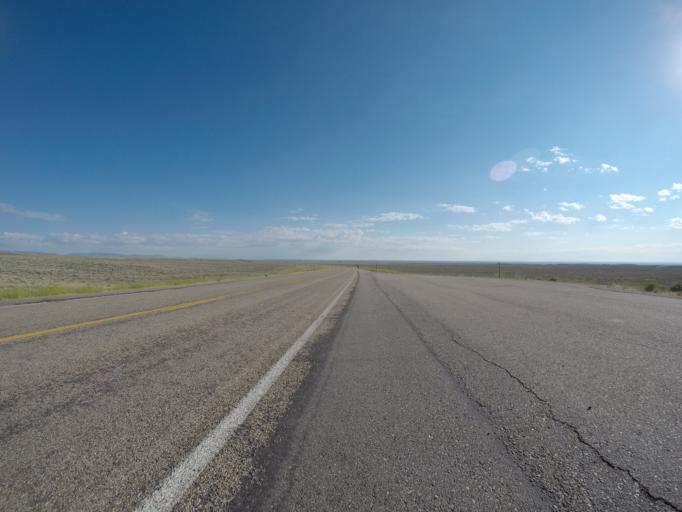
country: US
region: Wyoming
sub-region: Lincoln County
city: Kemmerer
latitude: 42.0204
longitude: -110.1535
